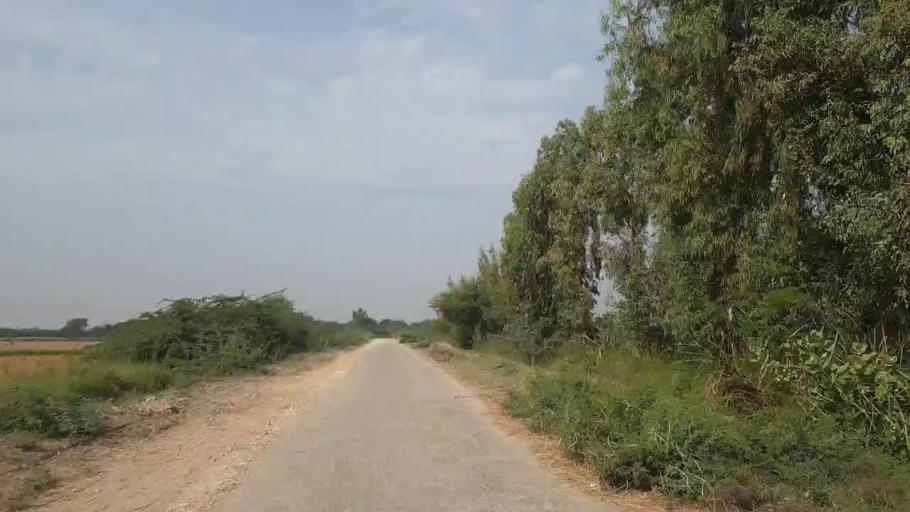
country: PK
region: Sindh
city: Tando Bago
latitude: 24.9248
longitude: 68.9899
